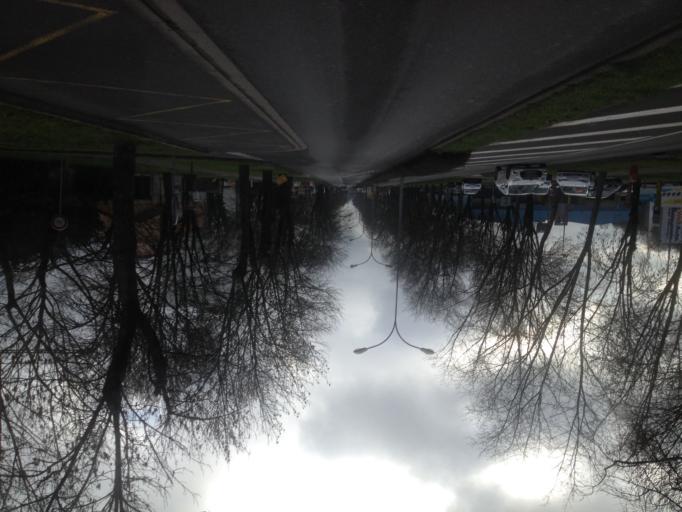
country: FR
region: Auvergne
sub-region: Departement de l'Allier
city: Creuzier-le-Vieux
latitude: 46.1485
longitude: 3.4143
